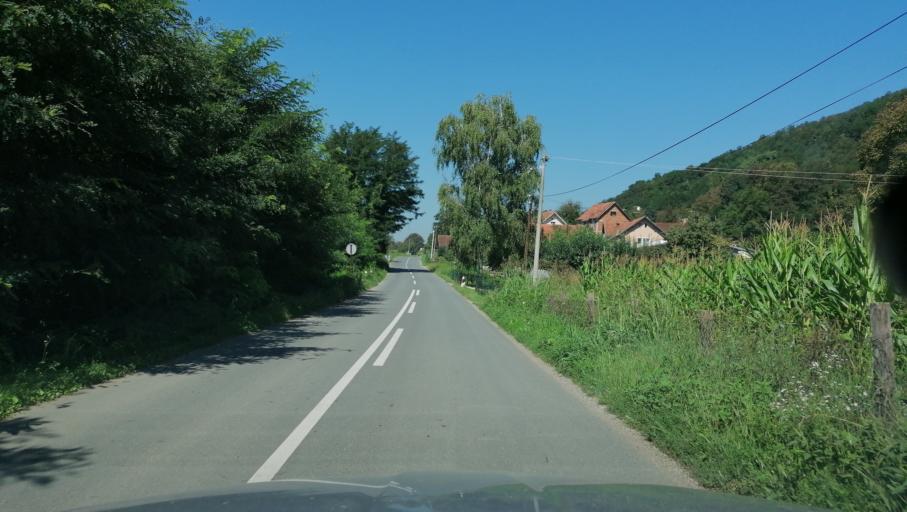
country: RS
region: Central Serbia
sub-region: Raski Okrug
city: Vrnjacka Banja
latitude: 43.6632
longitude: 20.9220
